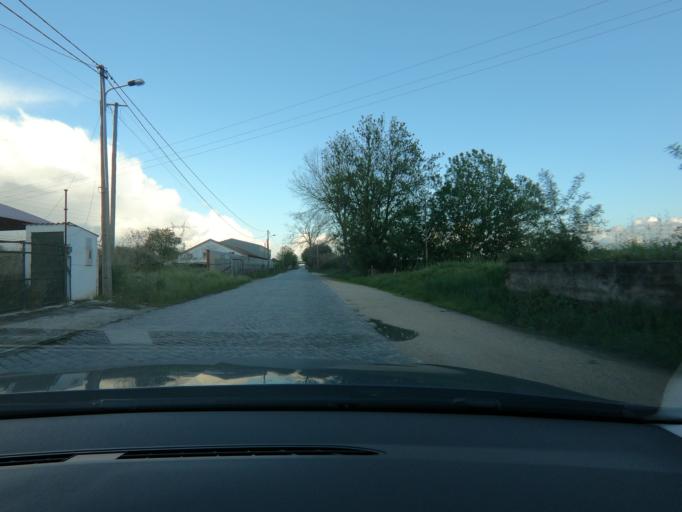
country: PT
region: Lisbon
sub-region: Alenquer
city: Carregado
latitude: 39.0141
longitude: -8.9703
